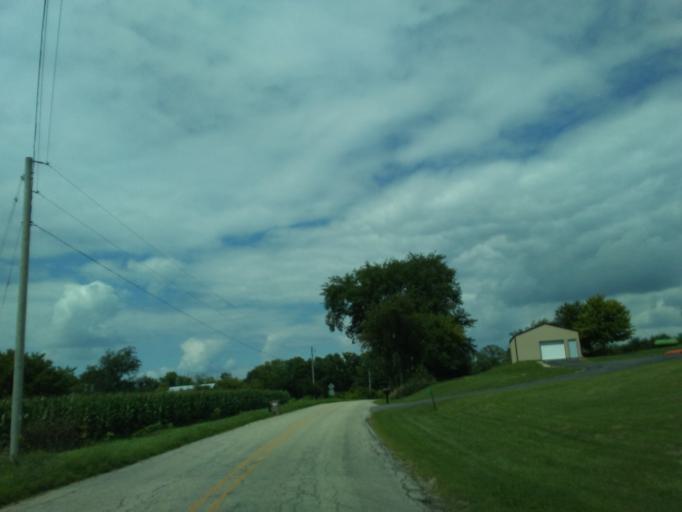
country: US
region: Wisconsin
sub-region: Dane County
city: Verona
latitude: 42.9975
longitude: -89.5779
